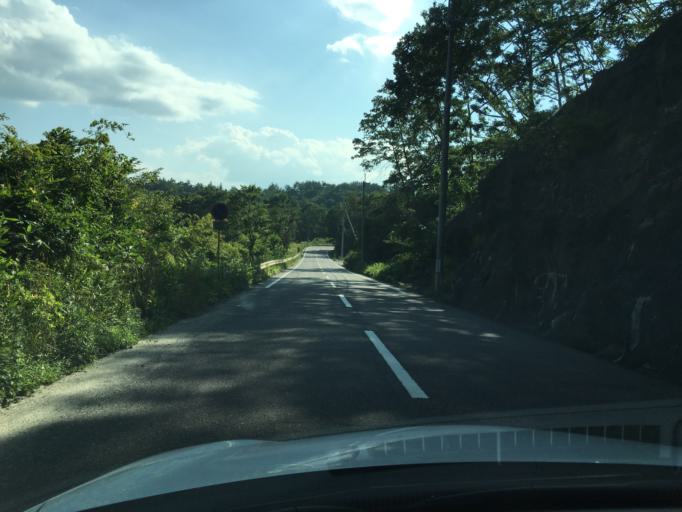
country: JP
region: Fukushima
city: Ishikawa
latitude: 37.1963
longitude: 140.4936
